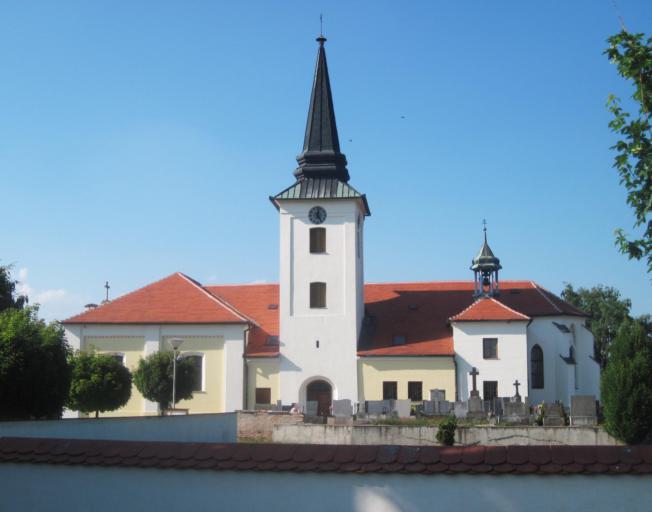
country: CZ
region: South Moravian
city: Moutnice
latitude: 49.0476
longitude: 16.7414
